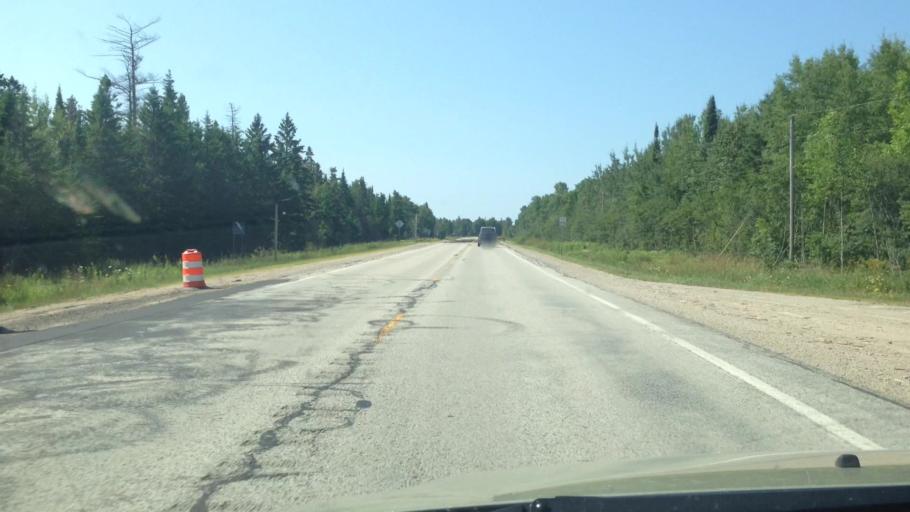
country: US
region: Michigan
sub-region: Delta County
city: Escanaba
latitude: 45.5535
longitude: -87.2690
